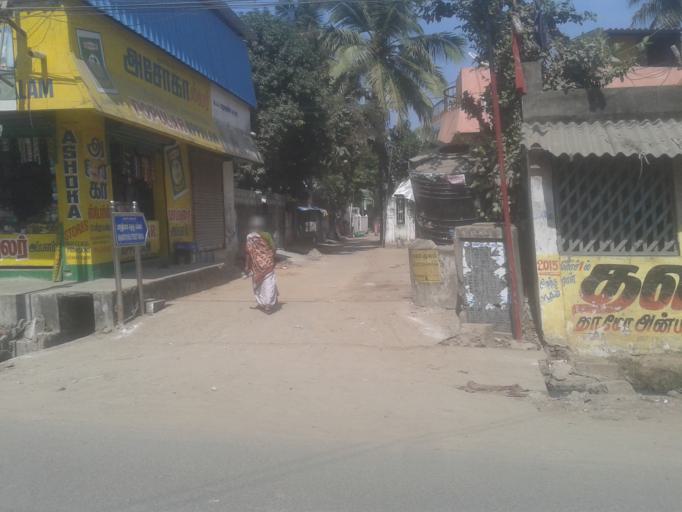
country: IN
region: Tamil Nadu
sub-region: Kancheepuram
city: Pallavaram
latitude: 12.9722
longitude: 80.1381
